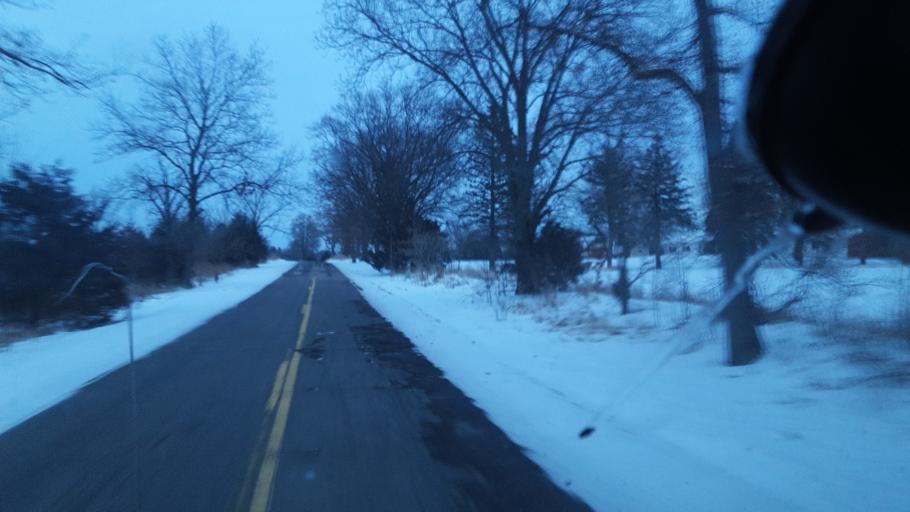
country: US
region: Michigan
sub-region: Ingham County
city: Stockbridge
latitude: 42.4083
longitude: -84.2914
